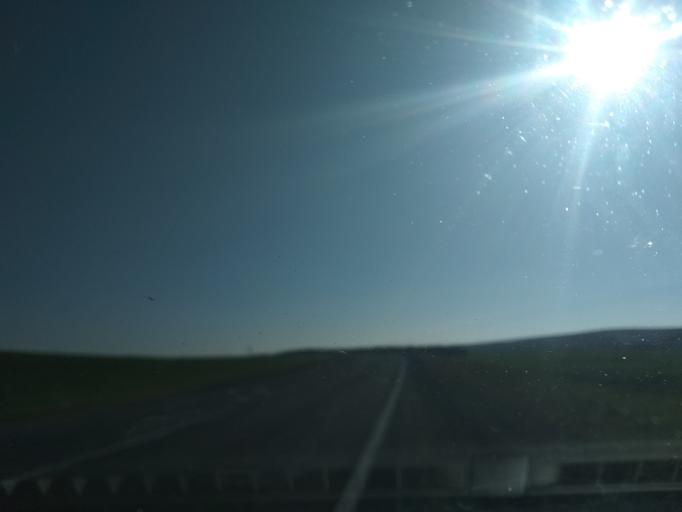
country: BY
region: Grodnenskaya
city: Zel'va
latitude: 53.1262
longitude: 25.0456
